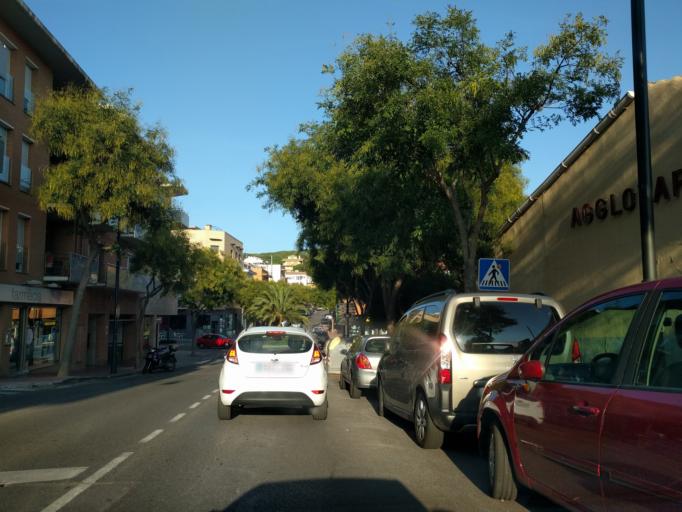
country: ES
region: Catalonia
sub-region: Provincia de Girona
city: Sant Feliu de Guixols
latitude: 41.7877
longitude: 3.0303
